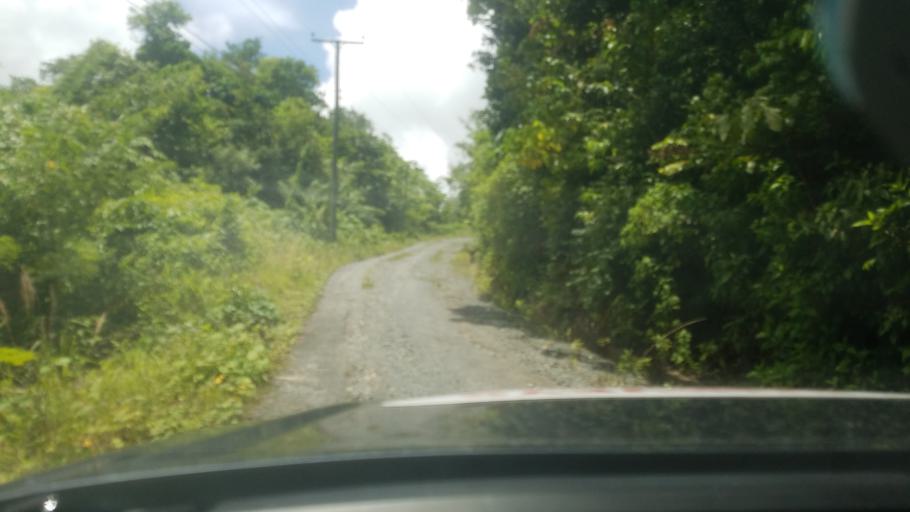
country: LC
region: Praslin
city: Praslin
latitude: 13.8680
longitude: -60.9150
